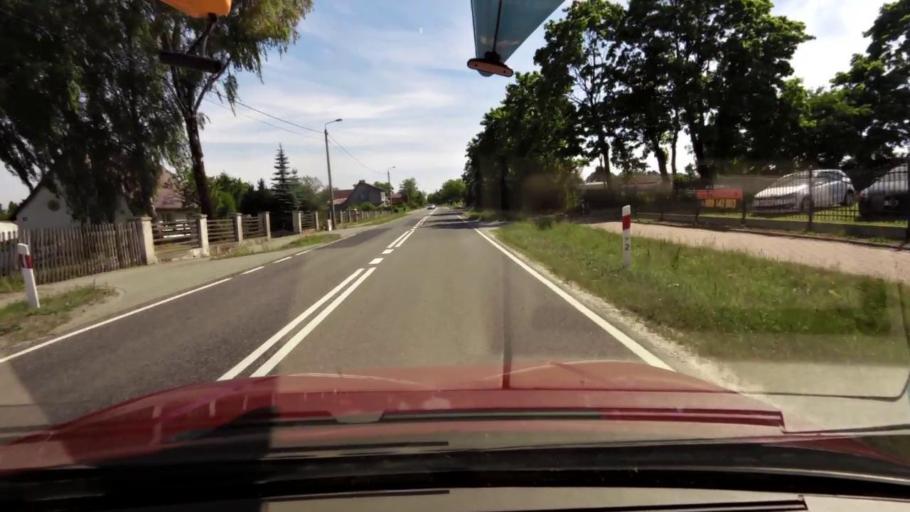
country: PL
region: Pomeranian Voivodeship
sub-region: Powiat slupski
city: Kobylnica
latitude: 54.4131
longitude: 17.0077
